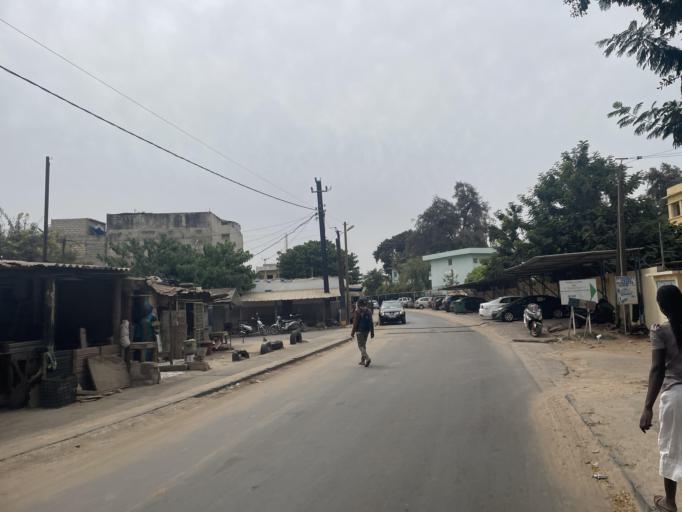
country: SN
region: Dakar
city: Grand Dakar
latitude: 14.7208
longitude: -17.4376
